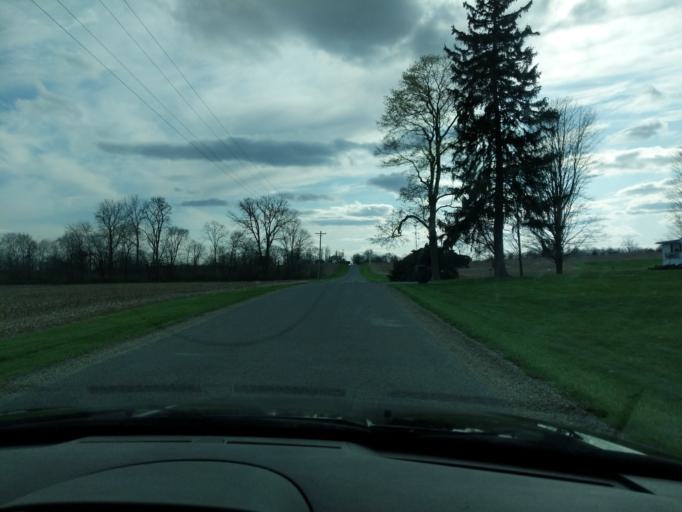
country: US
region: Ohio
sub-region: Champaign County
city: Urbana
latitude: 40.1445
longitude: -83.7034
